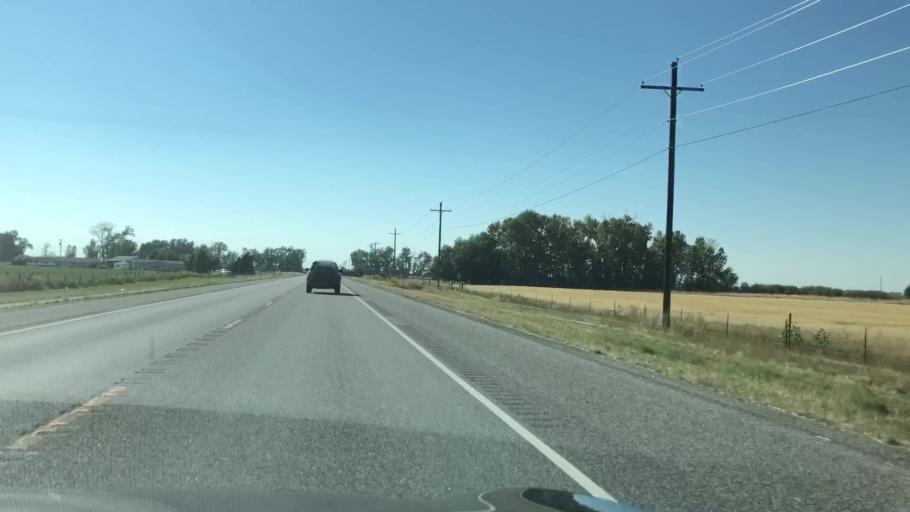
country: US
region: Montana
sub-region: Gallatin County
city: Belgrade
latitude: 45.7292
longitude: -111.1609
